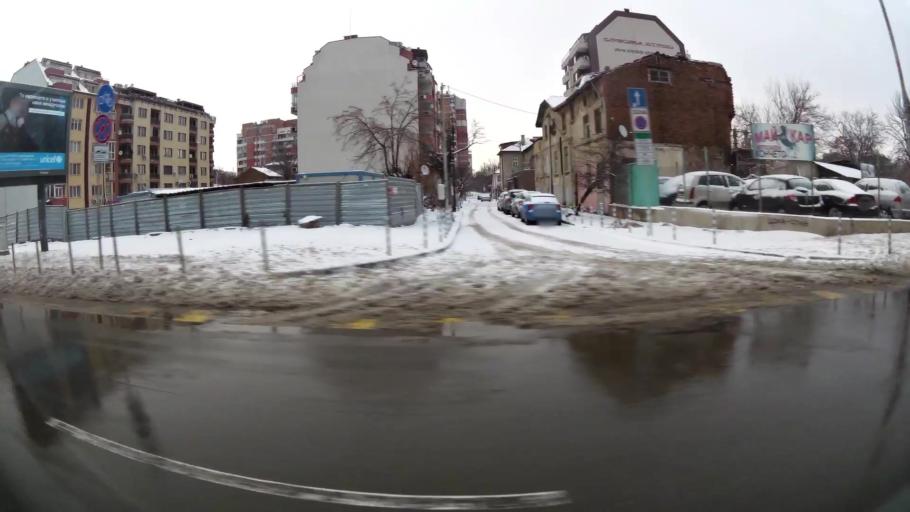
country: BG
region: Sofia-Capital
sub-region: Stolichna Obshtina
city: Sofia
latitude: 42.7013
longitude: 23.3025
